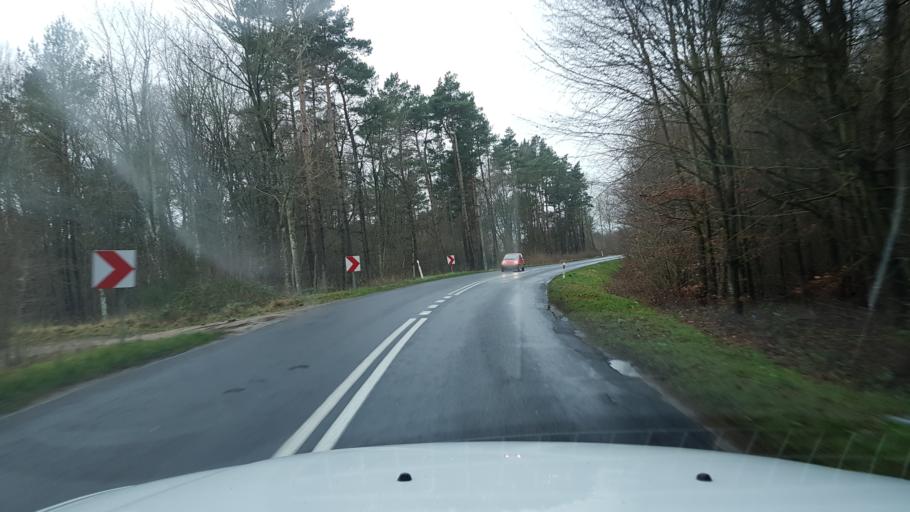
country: PL
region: West Pomeranian Voivodeship
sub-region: Powiat kolobrzeski
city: Grzybowo
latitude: 54.0731
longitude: 15.4323
